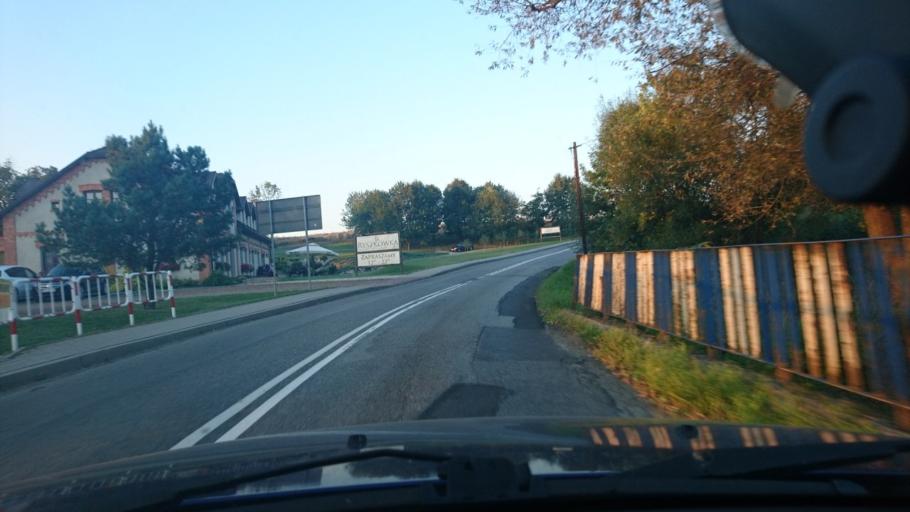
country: PL
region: Silesian Voivodeship
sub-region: Powiat bielski
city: Bestwina
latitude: 49.8977
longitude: 19.0673
